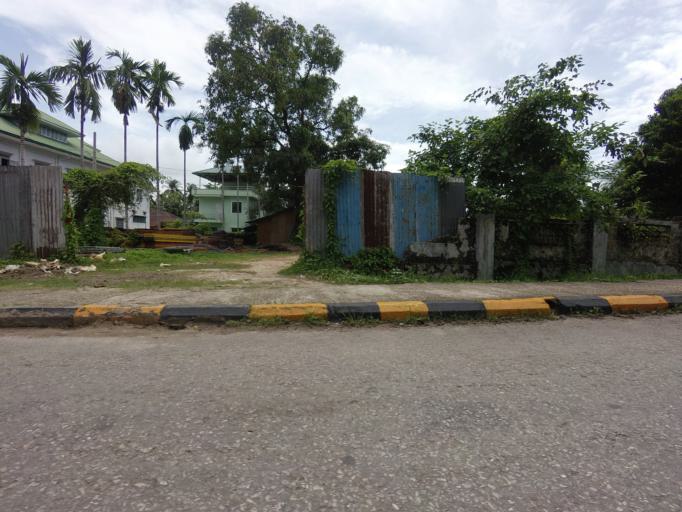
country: MM
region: Mon
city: Mawlamyine
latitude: 16.4767
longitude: 97.6245
